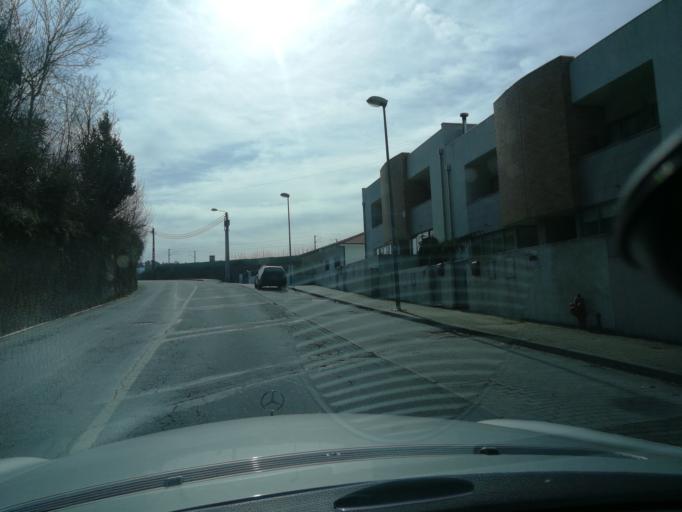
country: PT
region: Braga
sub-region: Vila Nova de Famalicao
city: Vila Nova de Famalicao
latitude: 41.4326
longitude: -8.5220
